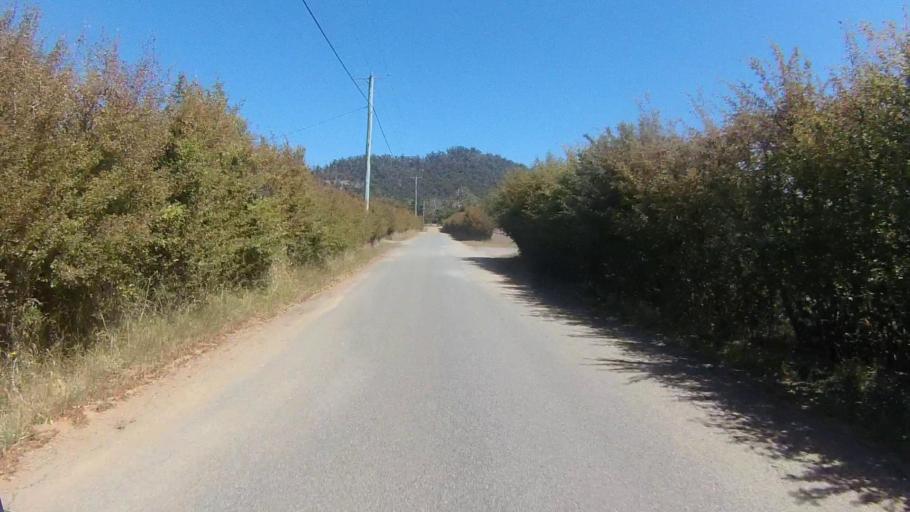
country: AU
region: Tasmania
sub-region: Clarence
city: Cambridge
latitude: -42.8452
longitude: 147.4581
